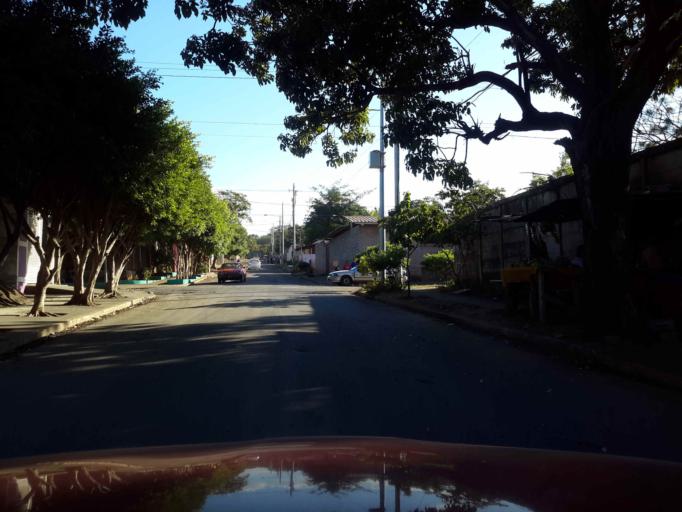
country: NI
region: Managua
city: Managua
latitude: 12.1125
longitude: -86.2934
